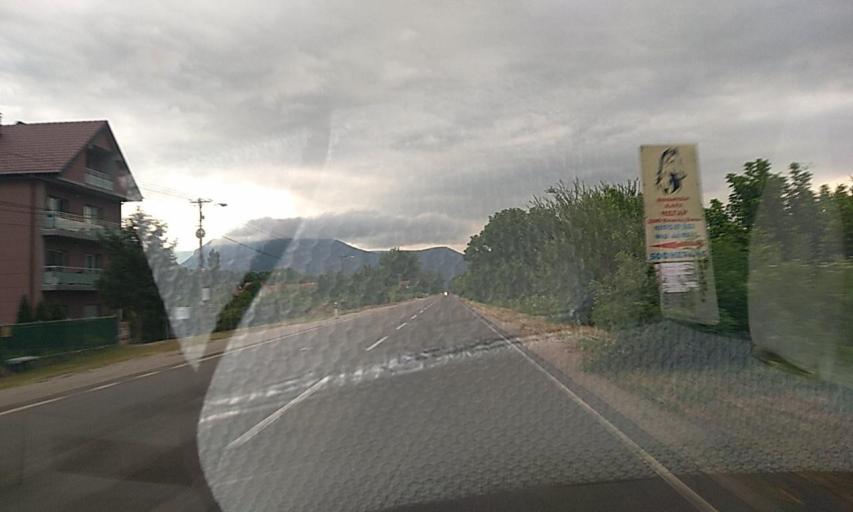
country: RS
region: Central Serbia
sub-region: Nisavski Okrug
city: Niska Banja
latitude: 43.3010
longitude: 22.0072
